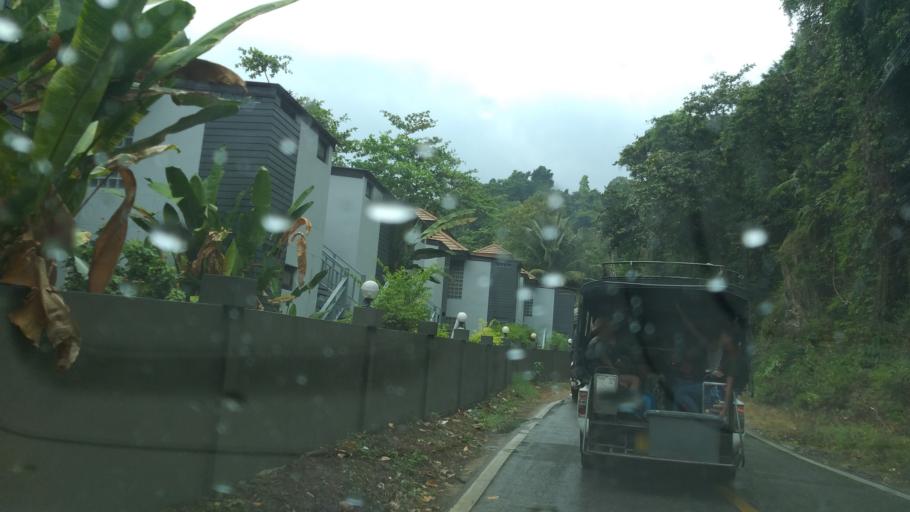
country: TH
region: Trat
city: Ko Chang Tai
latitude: 12.0096
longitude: 102.2923
